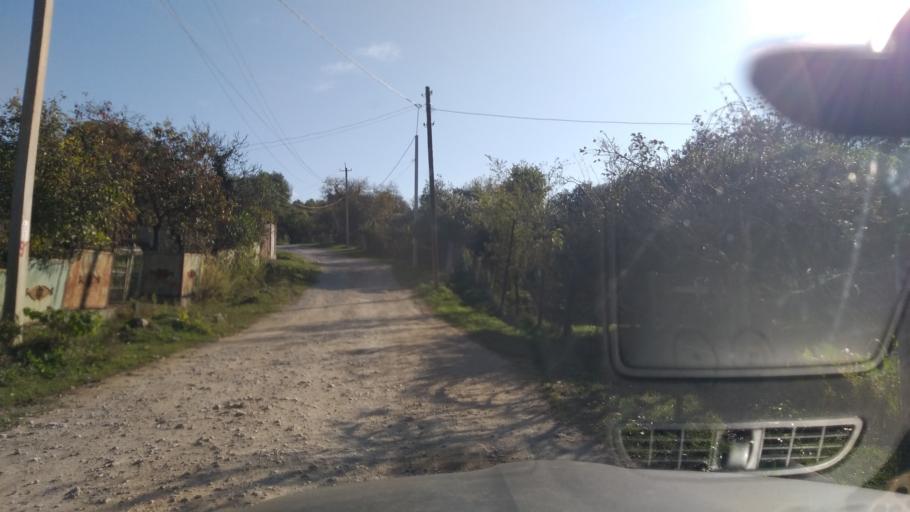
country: GE
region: Abkhazia
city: Stantsiya Novyy Afon
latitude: 43.0630
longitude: 40.8886
